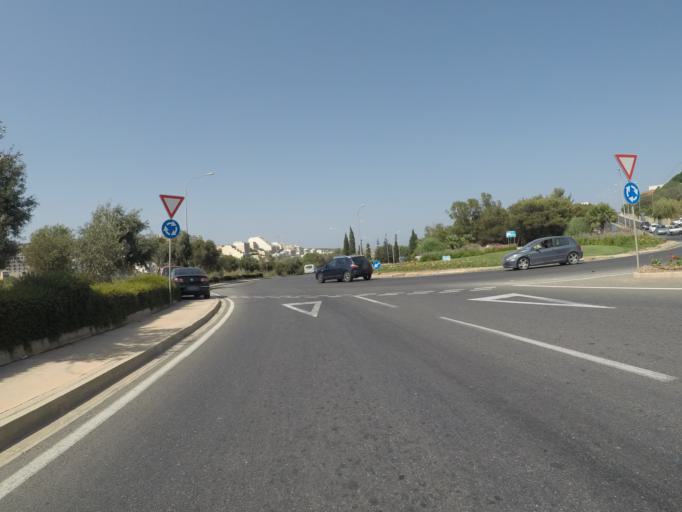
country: MT
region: Il-Mellieha
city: Mellieha
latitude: 35.9436
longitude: 14.3841
